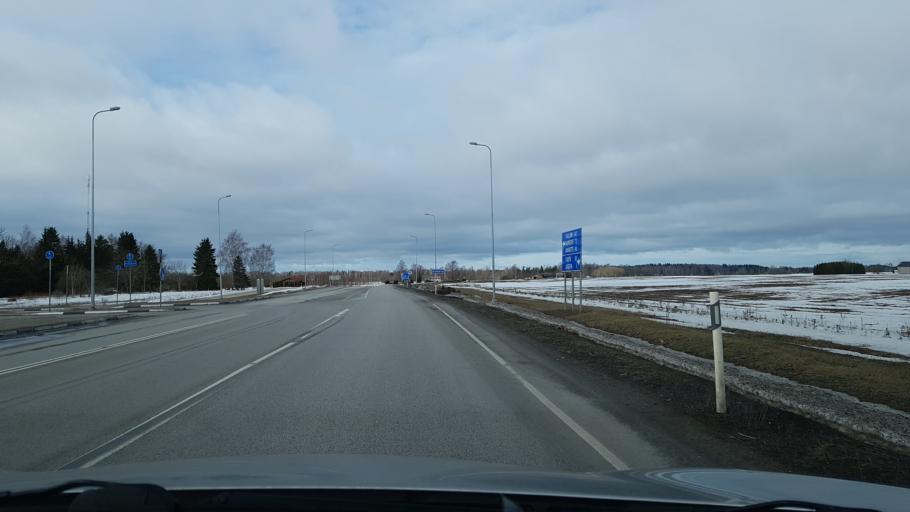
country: EE
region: Jogevamaa
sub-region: Jogeva linn
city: Jogeva
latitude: 58.7503
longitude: 26.3519
